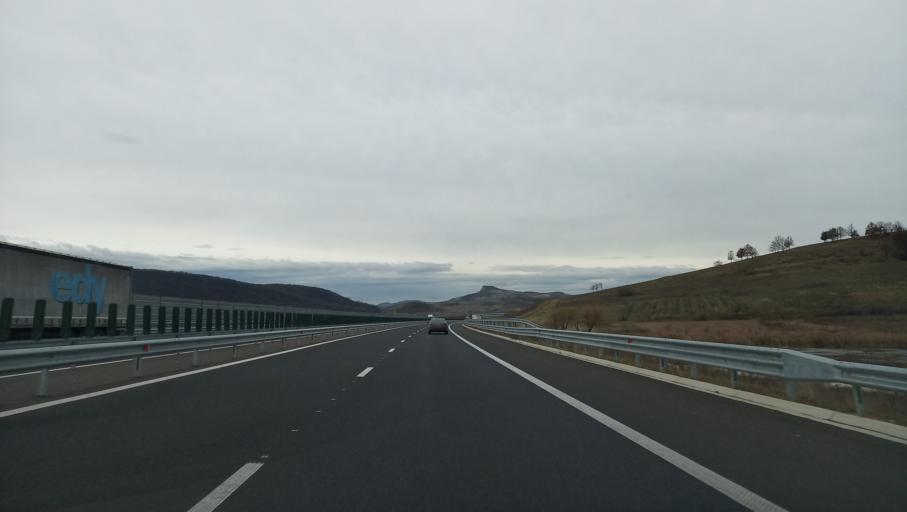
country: RO
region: Hunedoara
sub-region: Comuna Branisca
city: Branisca
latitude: 45.9262
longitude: 22.7719
